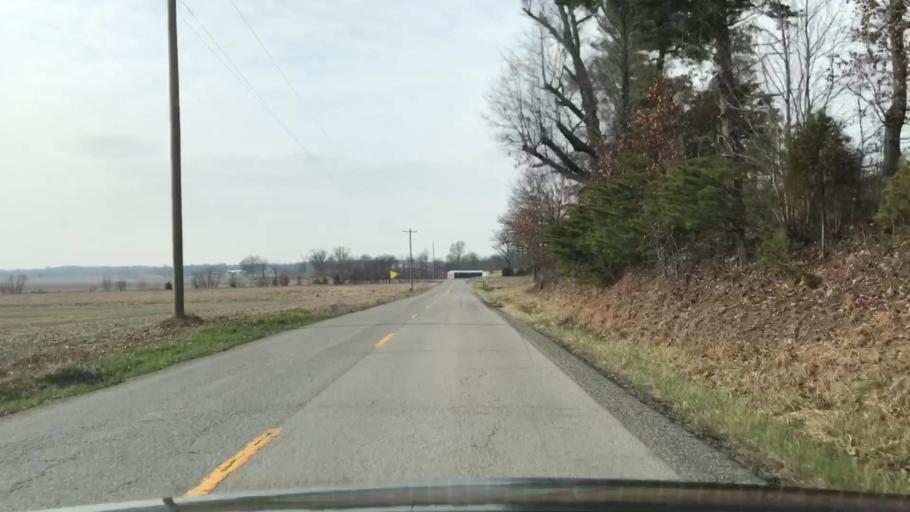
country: US
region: Kentucky
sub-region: Webster County
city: Sebree
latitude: 37.5147
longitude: -87.4083
